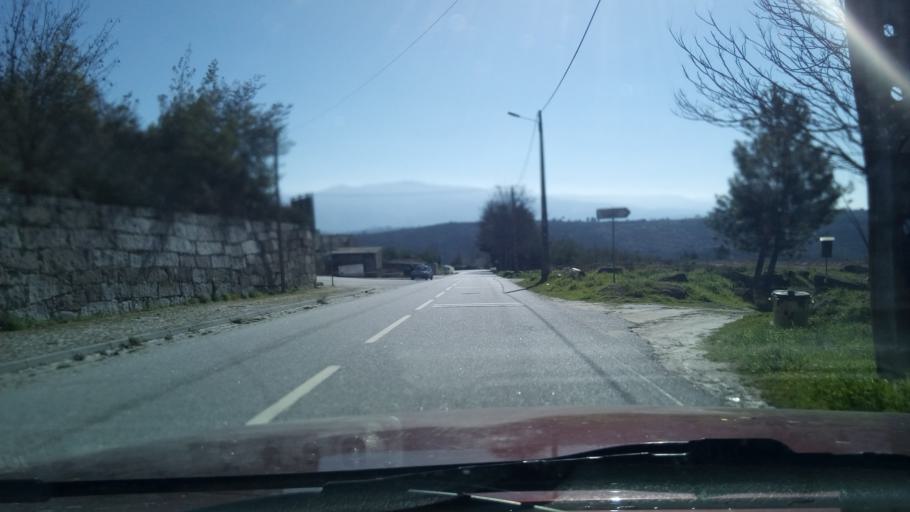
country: PT
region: Guarda
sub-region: Fornos de Algodres
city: Fornos de Algodres
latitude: 40.6116
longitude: -7.5336
